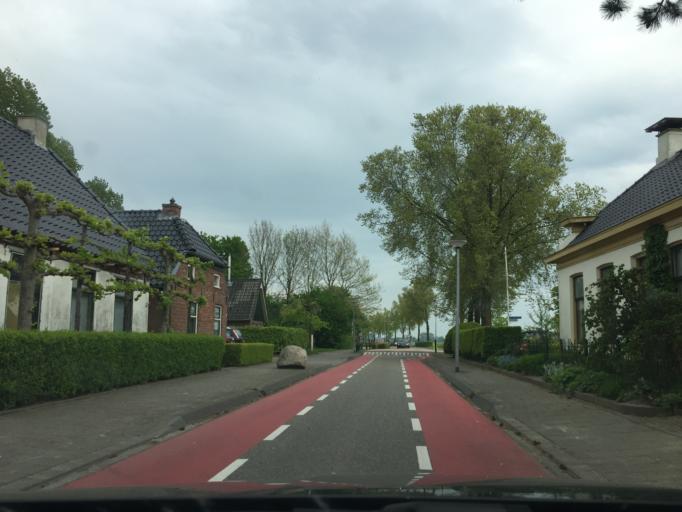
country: NL
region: Groningen
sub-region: Gemeente Zuidhorn
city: Noordhorn
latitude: 53.2736
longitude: 6.4278
